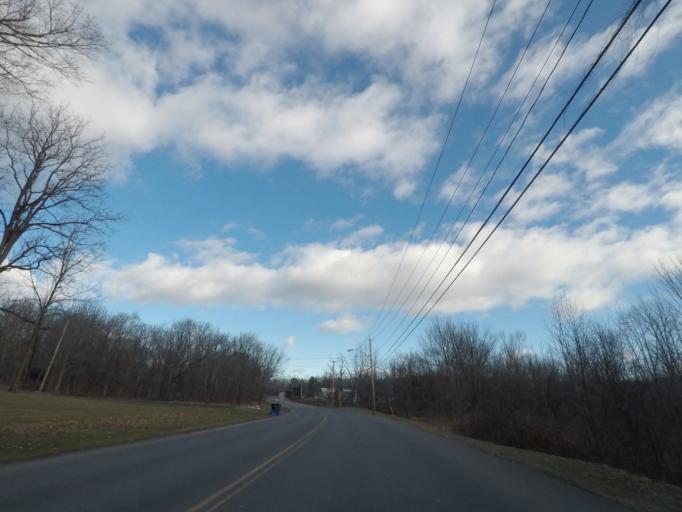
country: US
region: New York
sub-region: Albany County
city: Green Island
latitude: 42.7601
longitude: -73.6639
